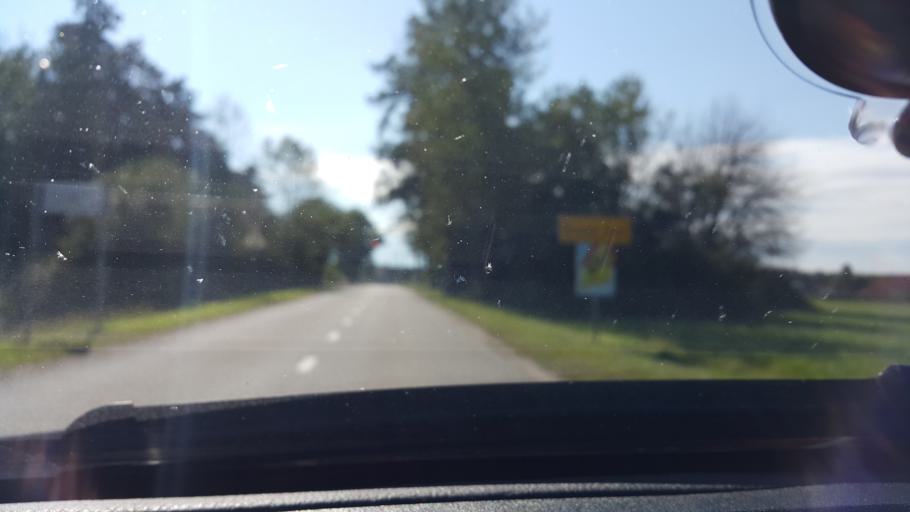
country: SI
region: Race-Fram
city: Race
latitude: 46.4708
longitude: 15.7112
